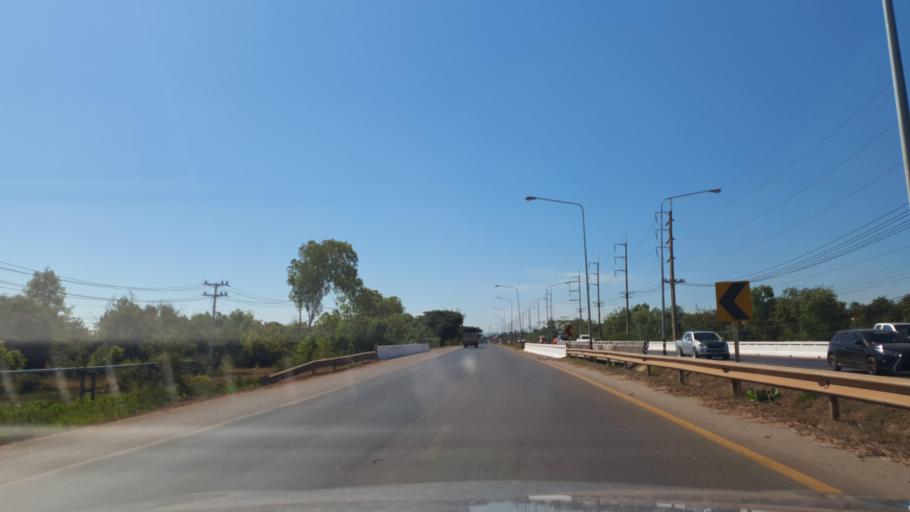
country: TH
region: Sakon Nakhon
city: Sakon Nakhon
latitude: 17.2600
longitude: 104.1170
